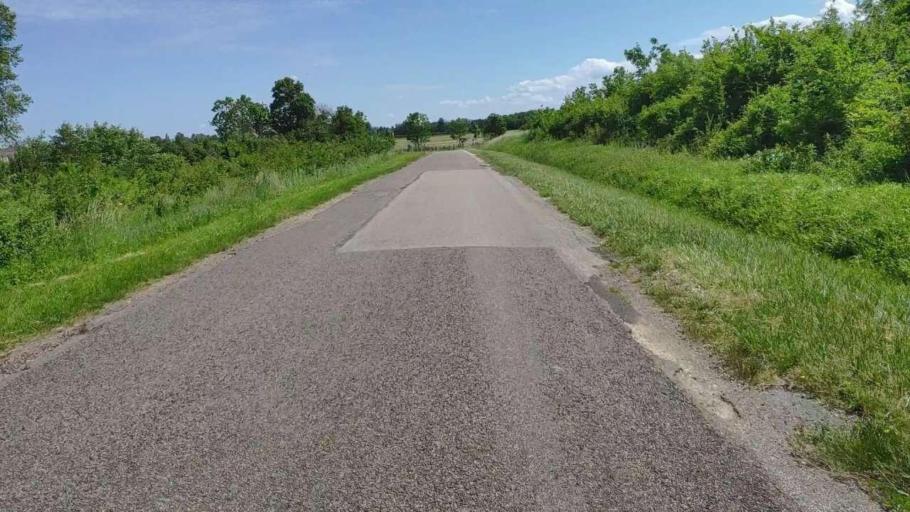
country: FR
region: Franche-Comte
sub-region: Departement du Jura
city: Bletterans
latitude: 46.7170
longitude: 5.4420
